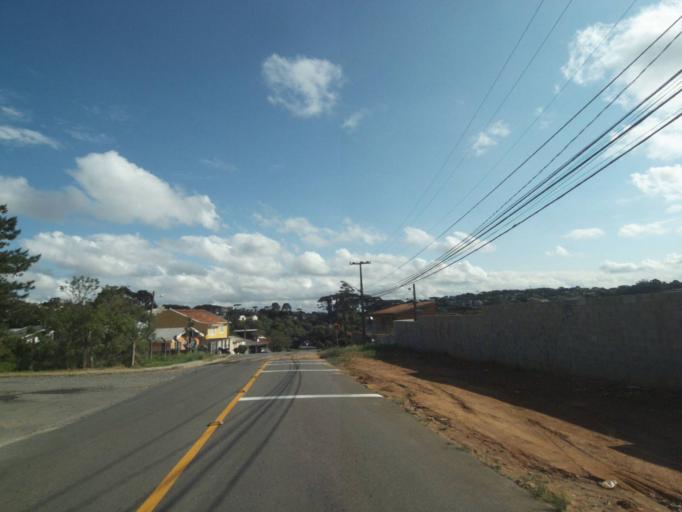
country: BR
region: Parana
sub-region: Curitiba
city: Curitiba
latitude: -25.3930
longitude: -49.3013
